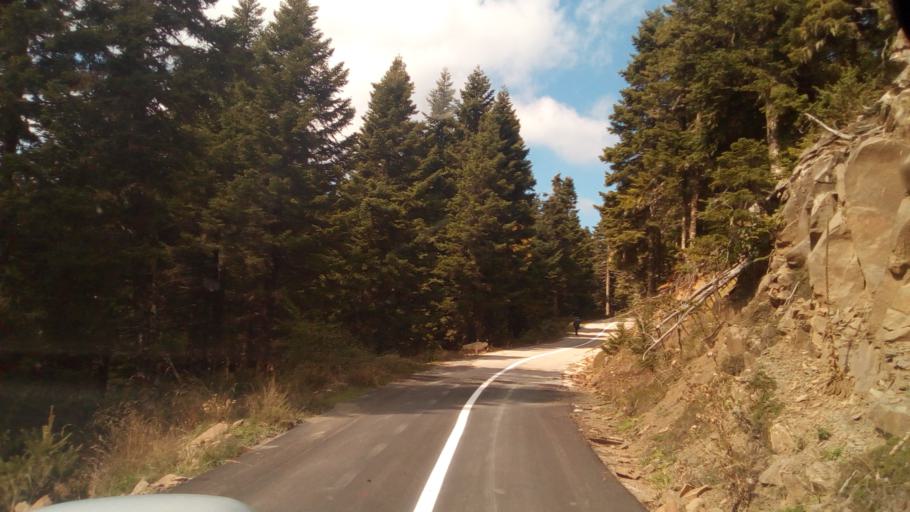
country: GR
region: West Greece
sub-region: Nomos Aitolias kai Akarnanias
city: Nafpaktos
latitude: 38.6392
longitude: 21.9315
